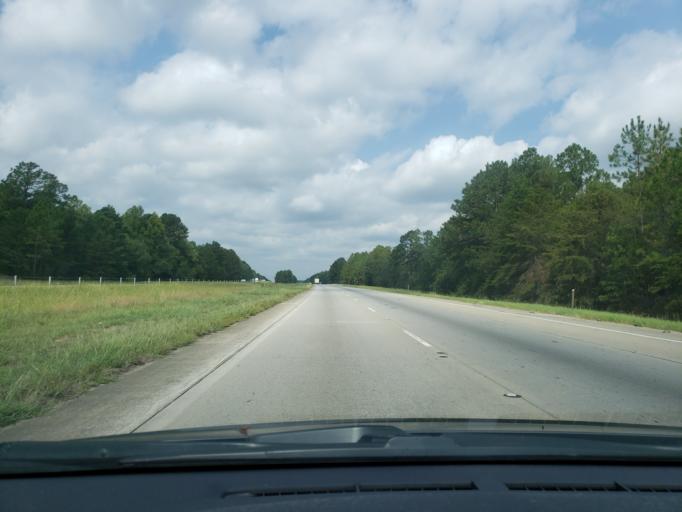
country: US
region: Georgia
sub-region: Emanuel County
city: Swainsboro
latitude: 32.4198
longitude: -82.3990
